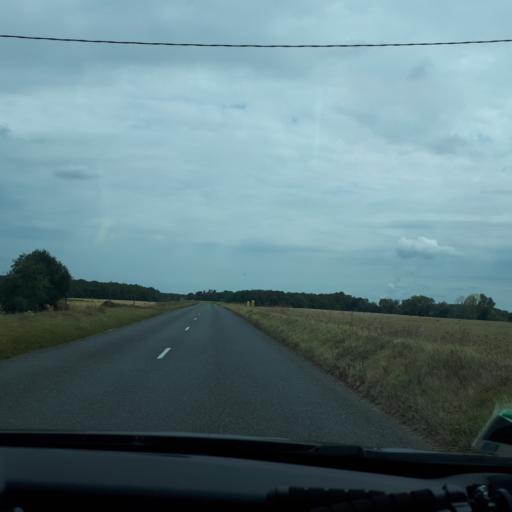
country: FR
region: Centre
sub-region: Departement du Loiret
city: Sully-sur-Loire
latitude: 47.7730
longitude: 2.4072
